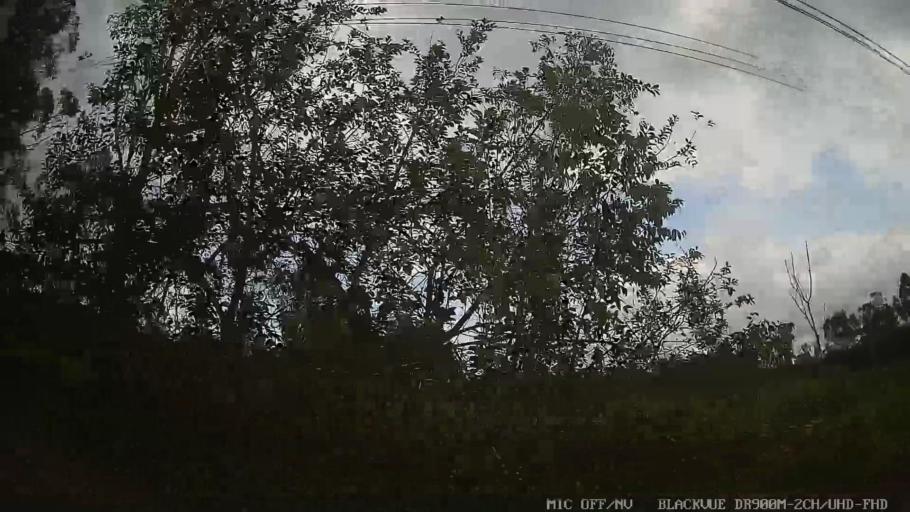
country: BR
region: Sao Paulo
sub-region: Suzano
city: Suzano
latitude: -23.5312
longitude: -46.2623
